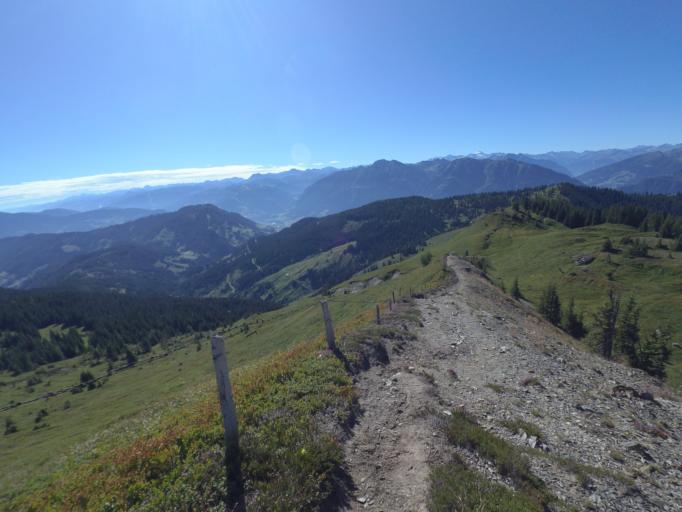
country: AT
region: Salzburg
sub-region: Politischer Bezirk Sankt Johann im Pongau
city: Goldegg
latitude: 47.3651
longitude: 13.0696
